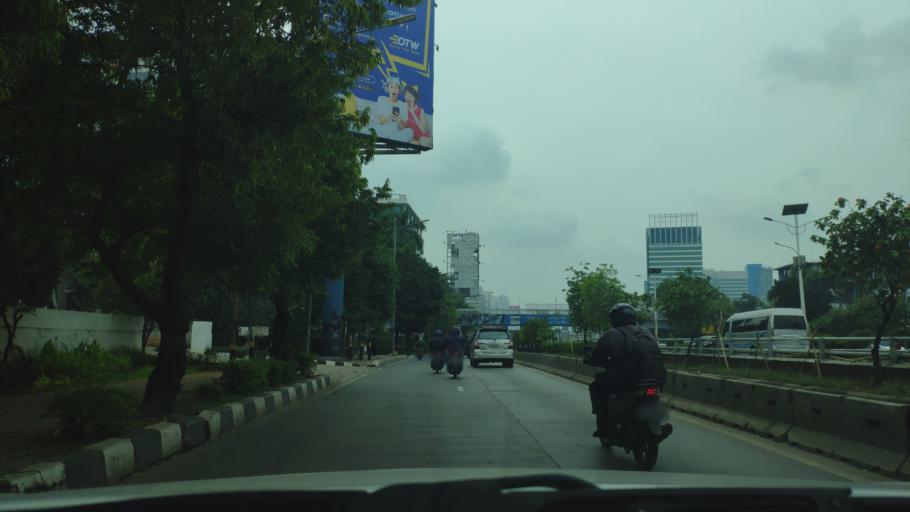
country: ID
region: Jakarta Raya
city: Jakarta
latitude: -6.1982
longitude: 106.7979
